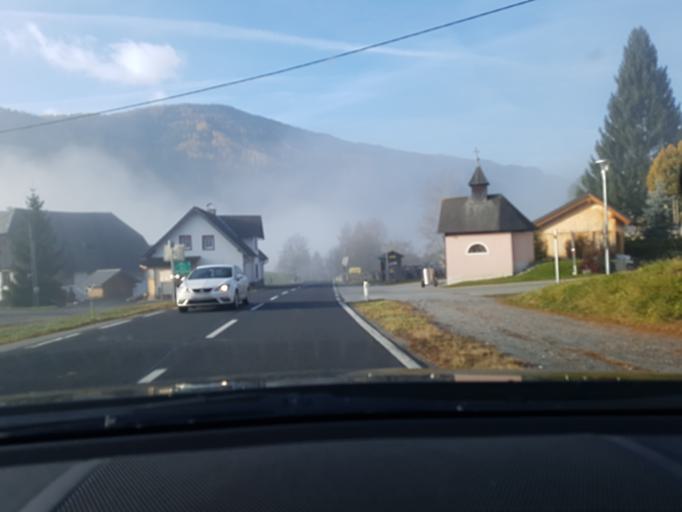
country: AT
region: Styria
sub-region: Politischer Bezirk Murau
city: Schoder
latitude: 47.1574
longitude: 14.1134
